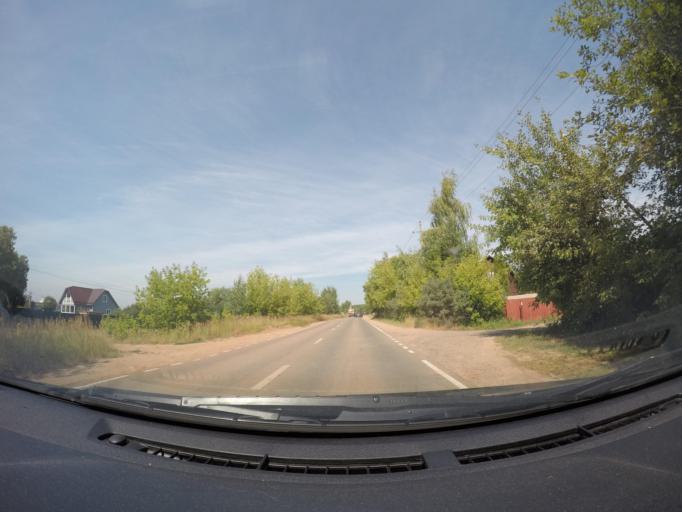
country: RU
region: Moskovskaya
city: Rechitsy
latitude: 55.6218
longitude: 38.4381
